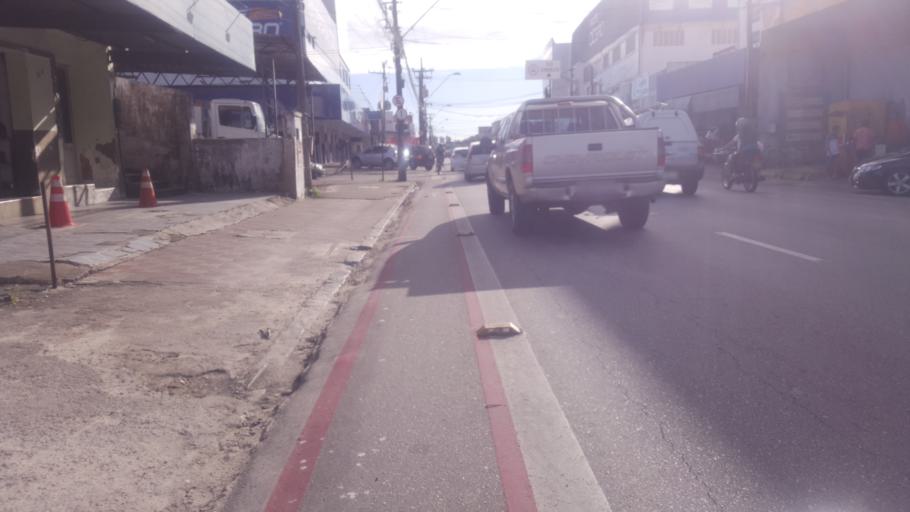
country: BR
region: Ceara
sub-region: Fortaleza
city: Fortaleza
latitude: -3.7644
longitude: -38.5485
